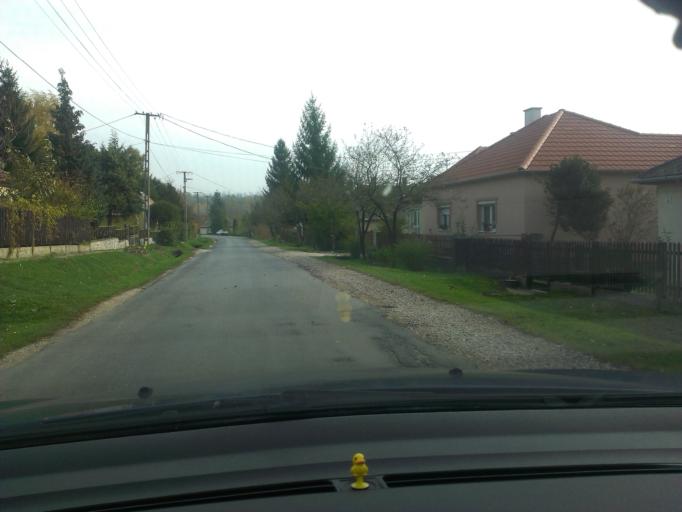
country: HU
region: Gyor-Moson-Sopron
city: Bakonyszentlaszlo
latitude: 47.3567
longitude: 17.8870
